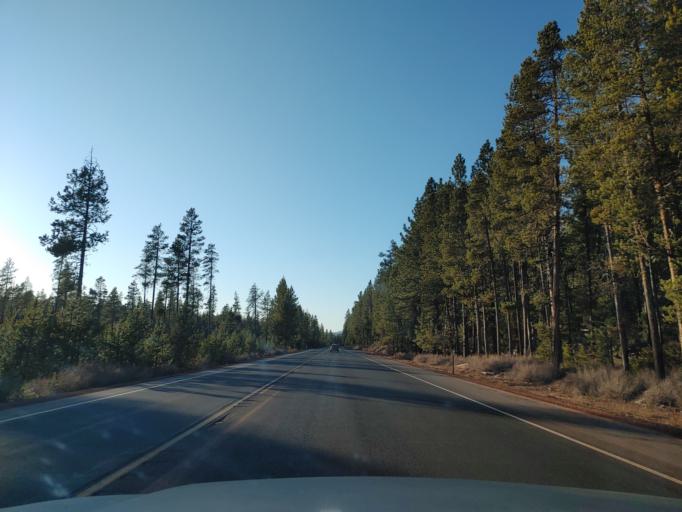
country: US
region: Oregon
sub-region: Deschutes County
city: La Pine
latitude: 43.4584
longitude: -121.8793
